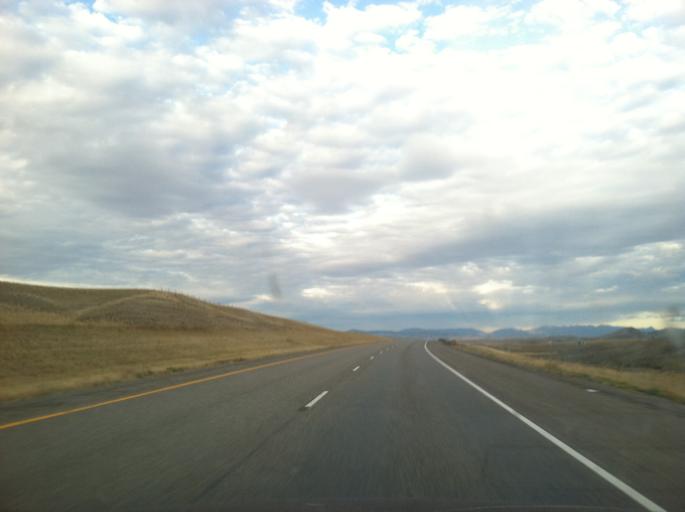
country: US
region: Montana
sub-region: Gallatin County
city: Three Forks
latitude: 45.9063
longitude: -111.7989
